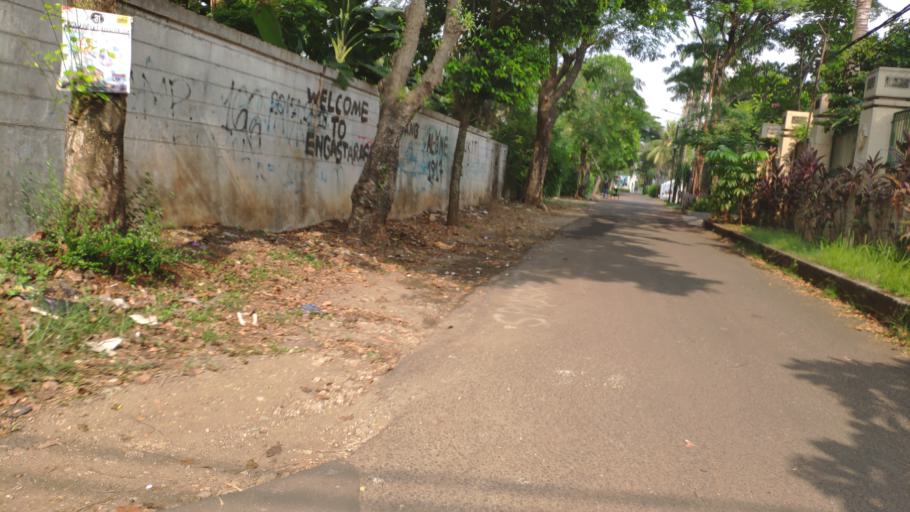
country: ID
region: West Java
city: Depok
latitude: -6.3238
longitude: 106.8141
